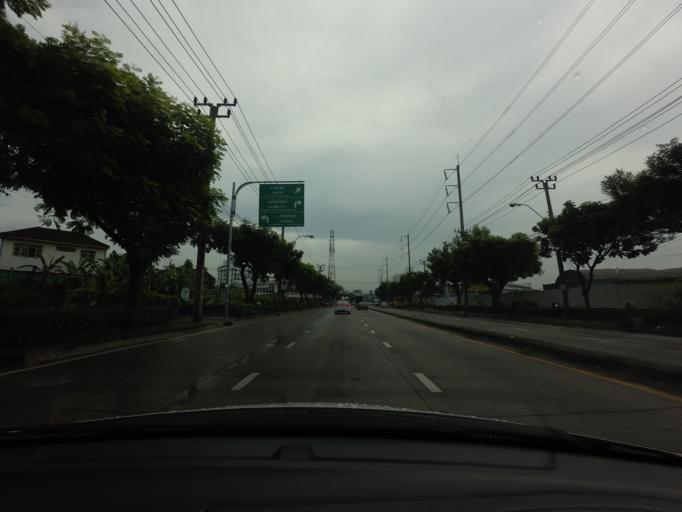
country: TH
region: Bangkok
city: Suan Luang
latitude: 13.7150
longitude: 100.6492
